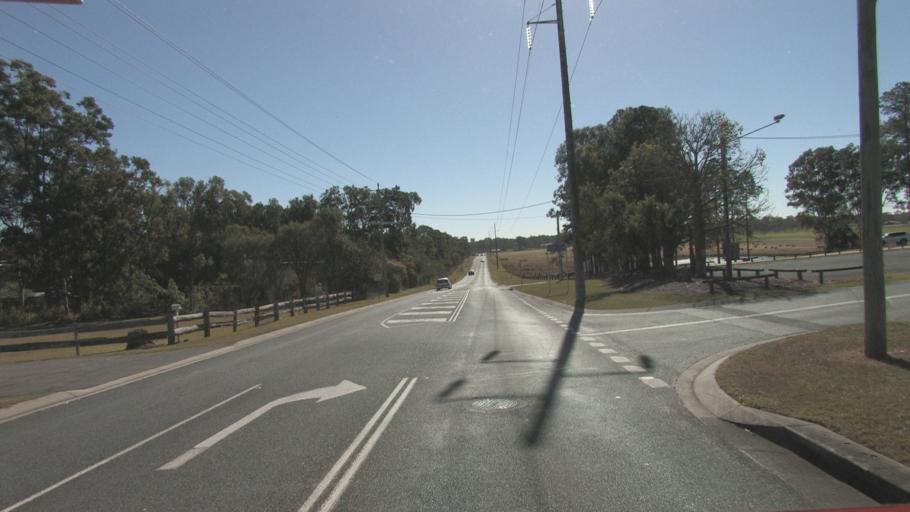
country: AU
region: Queensland
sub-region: Logan
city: Chambers Flat
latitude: -27.7581
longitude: 153.0914
